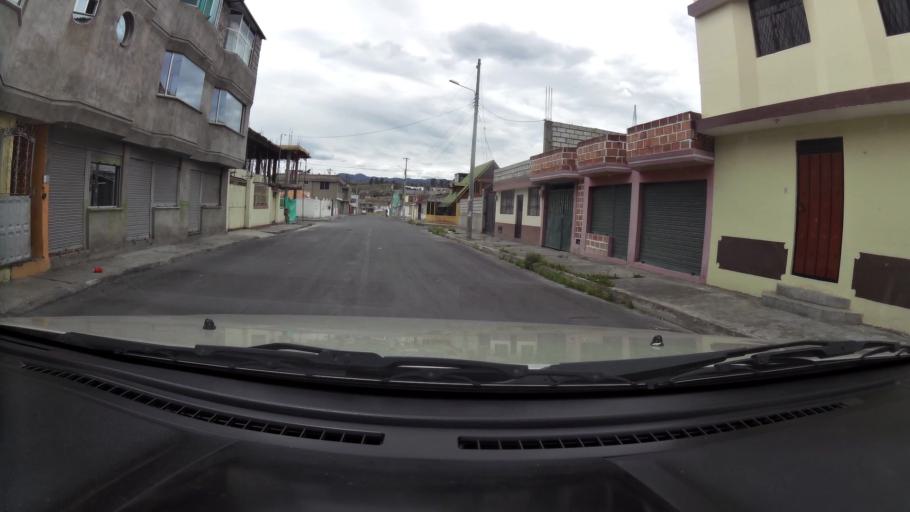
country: EC
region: Cotopaxi
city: Latacunga
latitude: -0.9565
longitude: -78.6048
